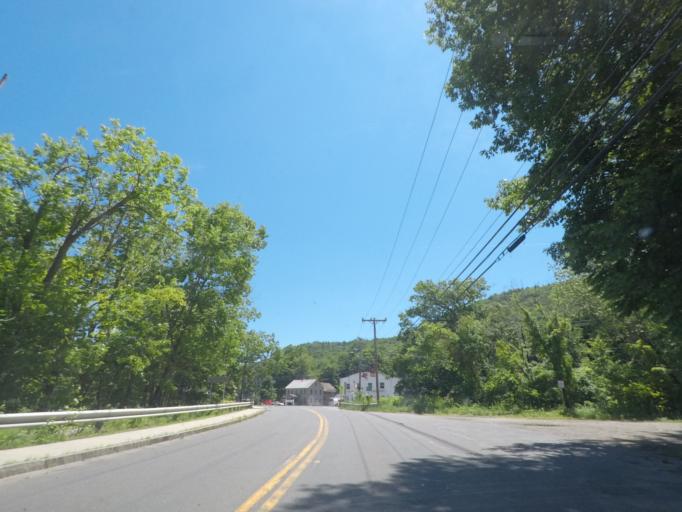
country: US
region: Massachusetts
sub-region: Berkshire County
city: Becket
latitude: 42.2783
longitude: -72.9806
